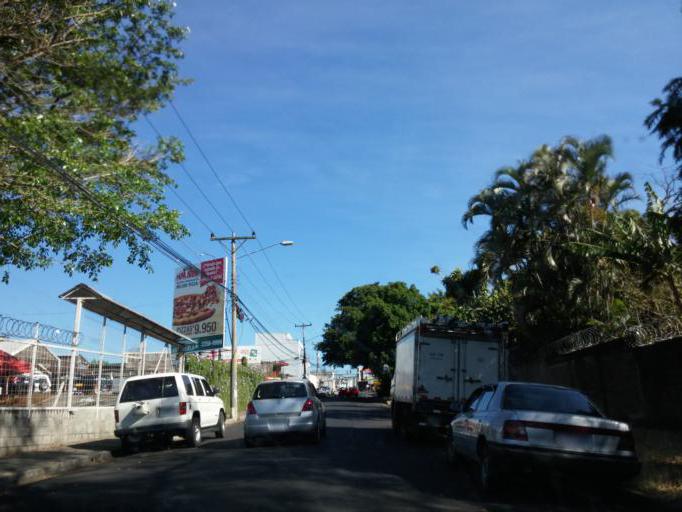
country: CR
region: Alajuela
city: Alajuela
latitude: 10.0104
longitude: -84.2126
